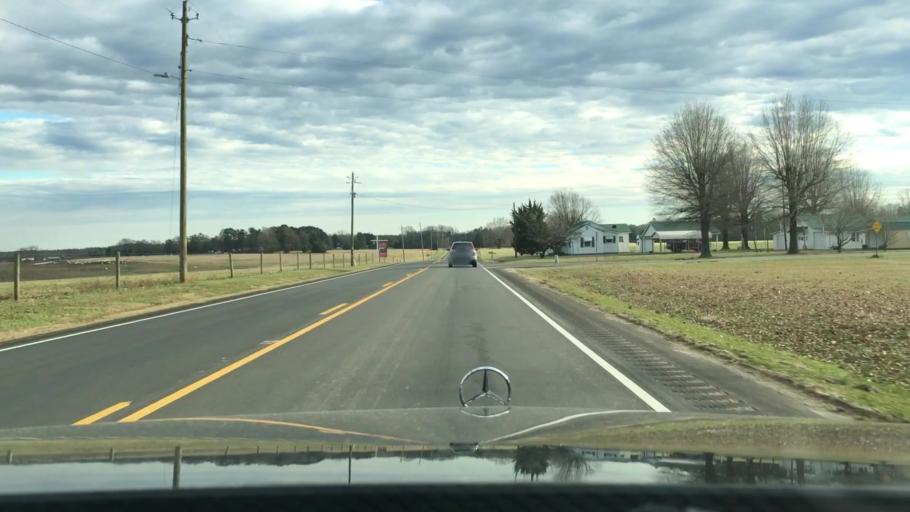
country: US
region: North Carolina
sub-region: Caswell County
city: Yanceyville
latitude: 36.3732
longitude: -79.2593
